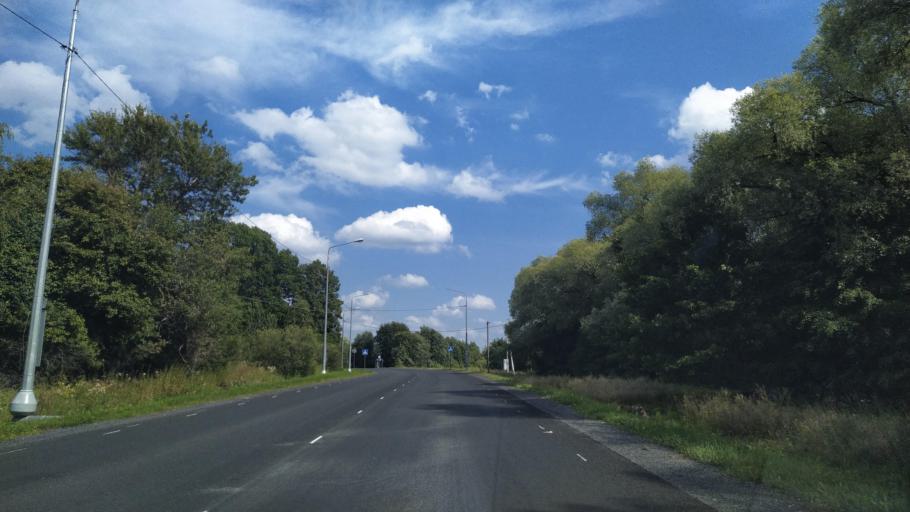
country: RU
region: Pskov
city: Porkhov
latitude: 57.7252
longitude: 29.2712
